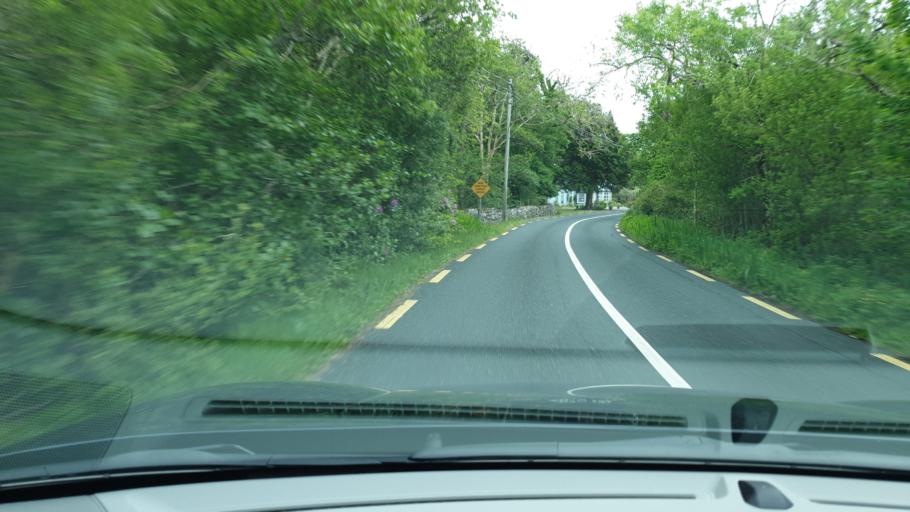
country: IE
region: Connaught
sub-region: County Galway
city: Clifden
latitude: 53.4398
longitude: -9.8684
